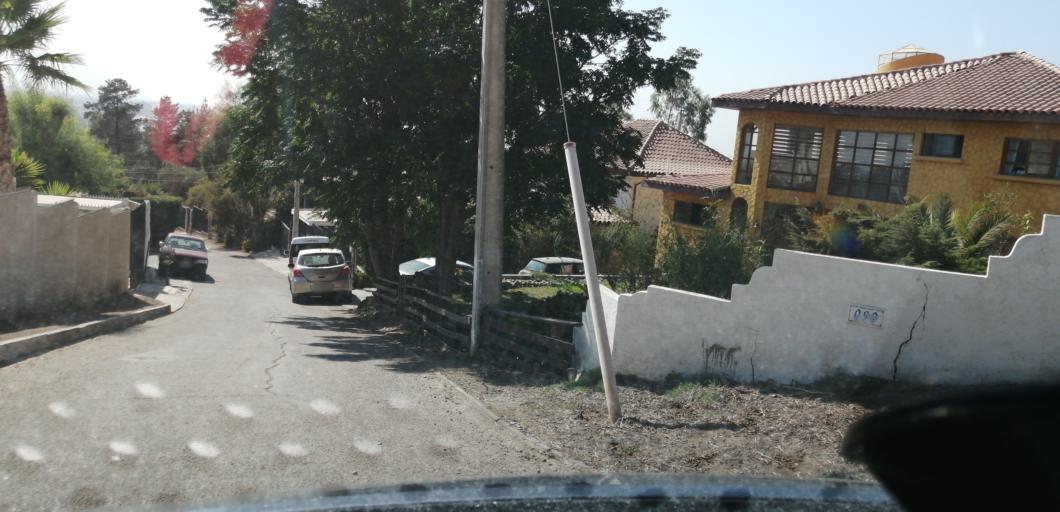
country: CL
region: Santiago Metropolitan
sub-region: Provincia de Santiago
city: Lo Prado
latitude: -33.4594
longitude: -70.8192
